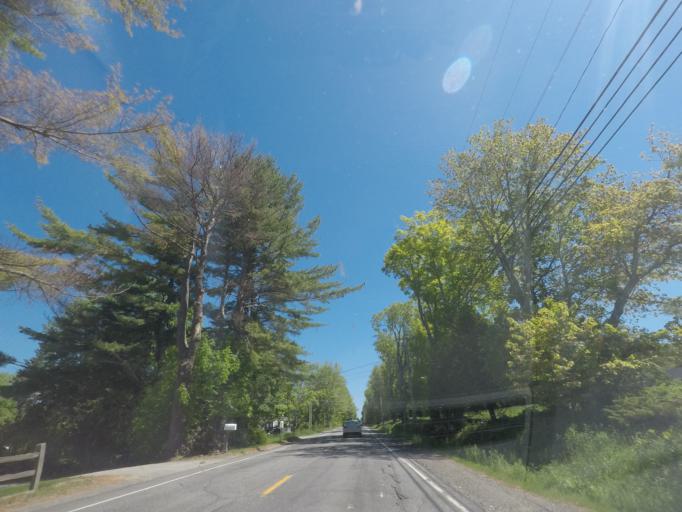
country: US
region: Maine
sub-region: Kennebec County
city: Manchester
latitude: 44.3063
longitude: -69.8802
